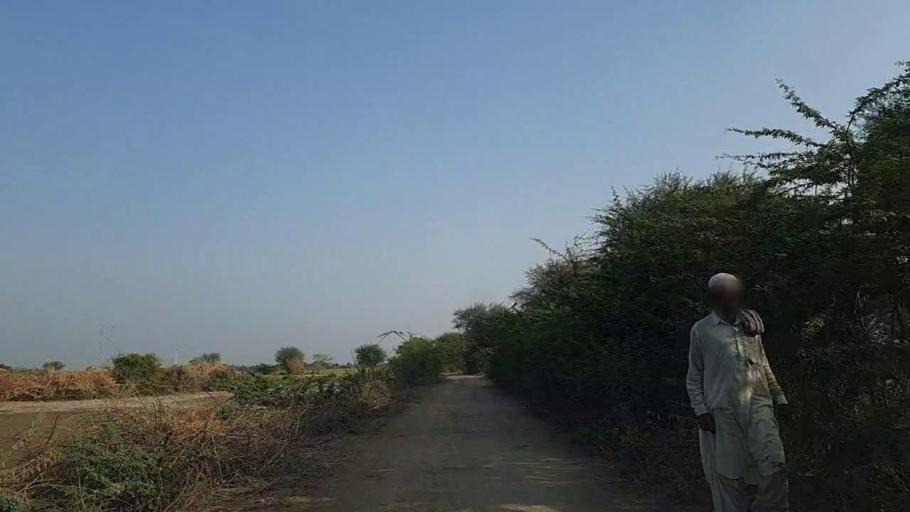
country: PK
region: Sindh
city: Dhoro Naro
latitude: 25.4927
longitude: 69.4963
